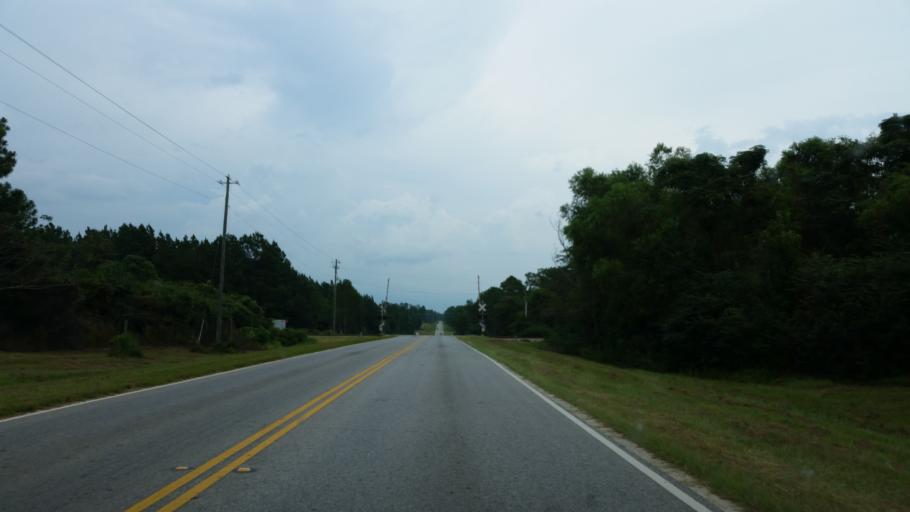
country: US
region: Florida
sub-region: Escambia County
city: Cantonment
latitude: 30.6519
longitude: -87.3183
